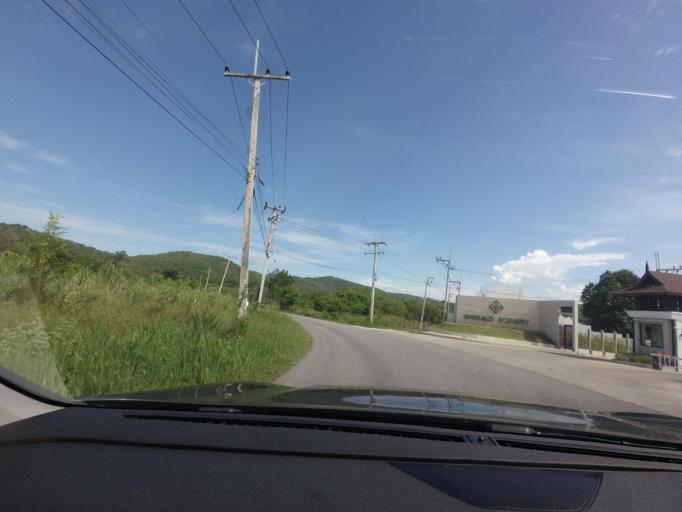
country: TH
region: Prachuap Khiri Khan
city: Hua Hin
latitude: 12.4982
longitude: 99.9370
